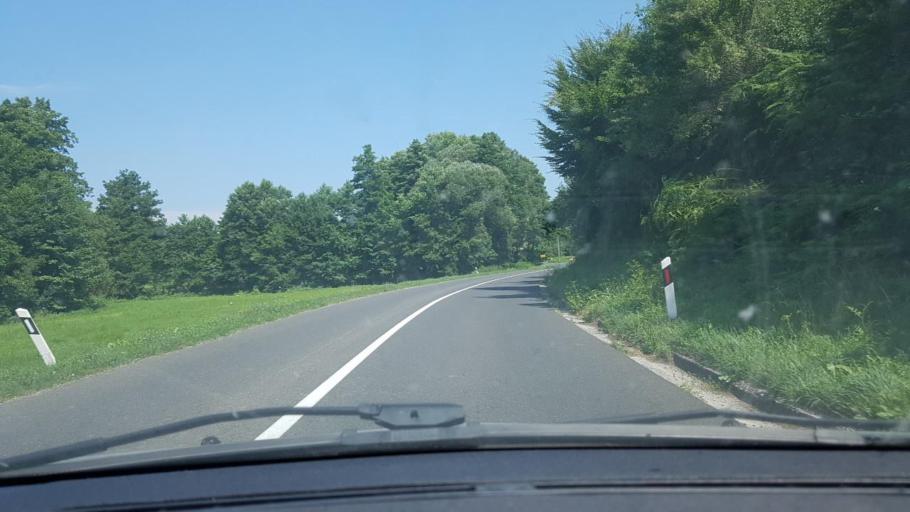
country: BA
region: Federation of Bosnia and Herzegovina
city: Velika Kladusa
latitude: 45.2381
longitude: 15.7364
